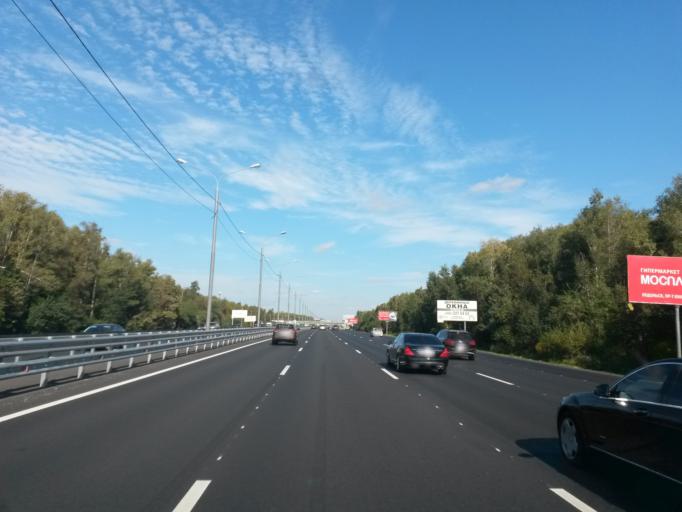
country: RU
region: Moskovskaya
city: Shcherbinka
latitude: 55.4967
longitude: 37.6109
